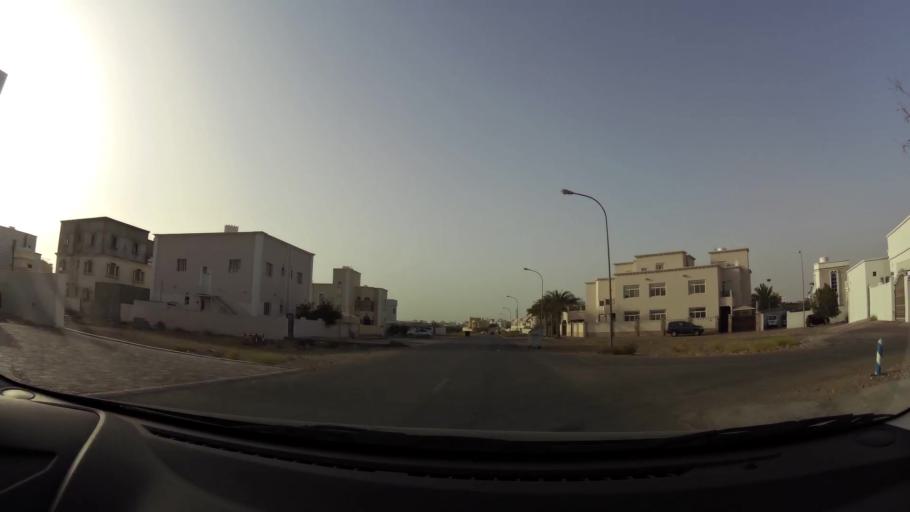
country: OM
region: Muhafazat Masqat
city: Bawshar
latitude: 23.5326
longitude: 58.3528
